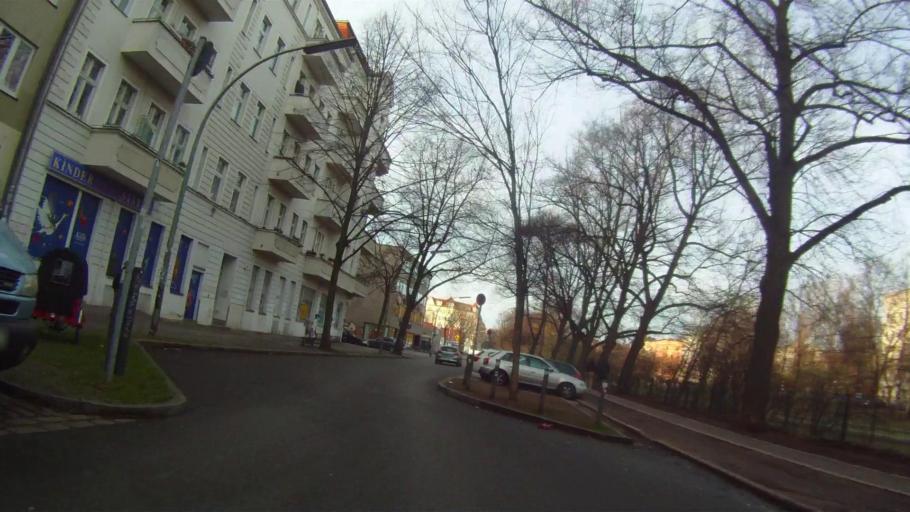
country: DE
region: Berlin
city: Berlin Treptow
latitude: 52.4915
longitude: 13.4345
